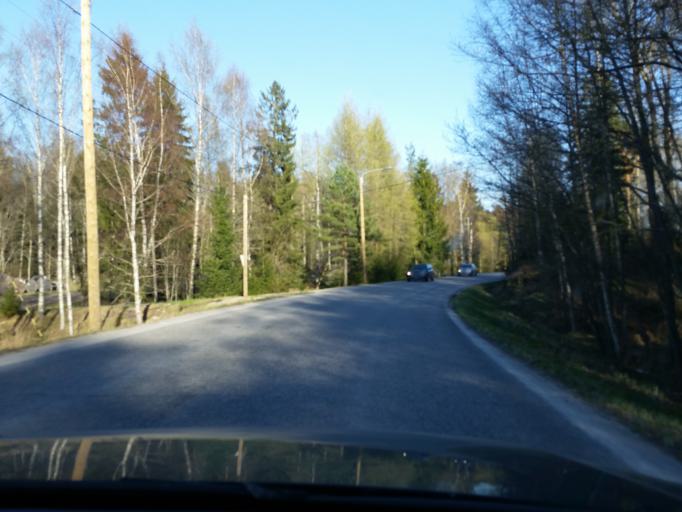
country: FI
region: Uusimaa
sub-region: Helsinki
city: Kirkkonummi
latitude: 60.1121
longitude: 24.5642
